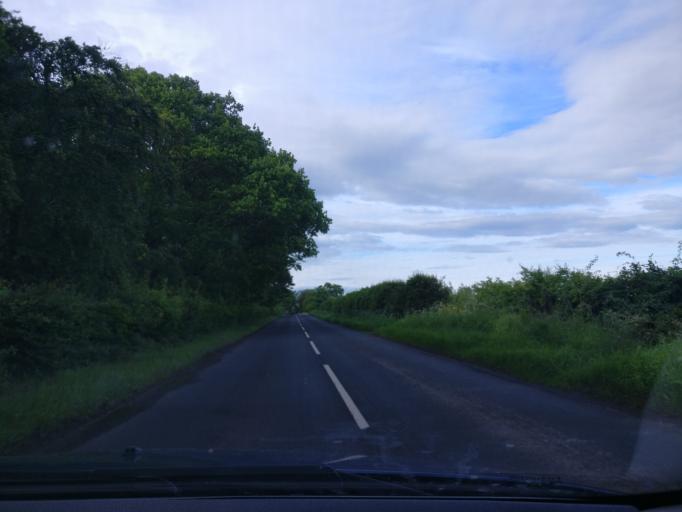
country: GB
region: Scotland
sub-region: East Lothian
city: Haddington
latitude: 55.9157
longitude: -2.7457
